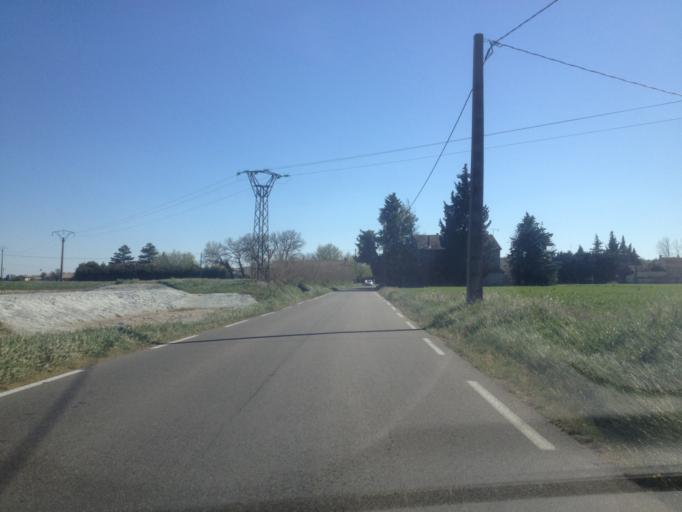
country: FR
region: Provence-Alpes-Cote d'Azur
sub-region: Departement du Vaucluse
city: Orange
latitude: 44.1516
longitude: 4.8253
